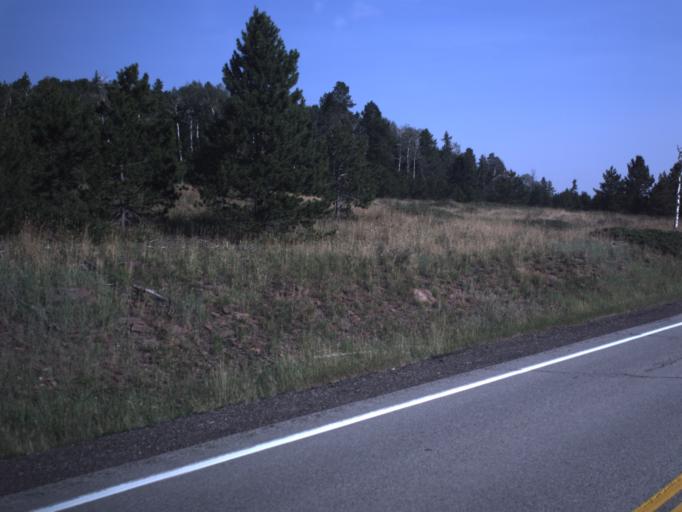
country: US
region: Utah
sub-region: Daggett County
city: Manila
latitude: 40.8391
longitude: -109.4645
